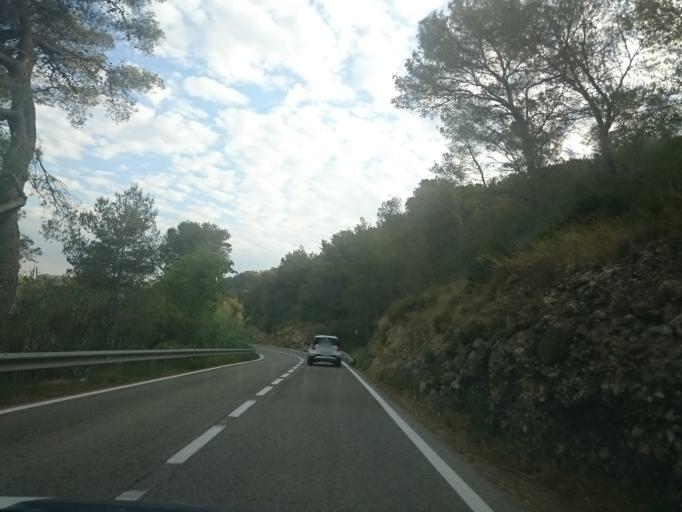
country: ES
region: Catalonia
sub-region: Provincia de Barcelona
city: Castellet
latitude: 41.2565
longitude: 1.6418
